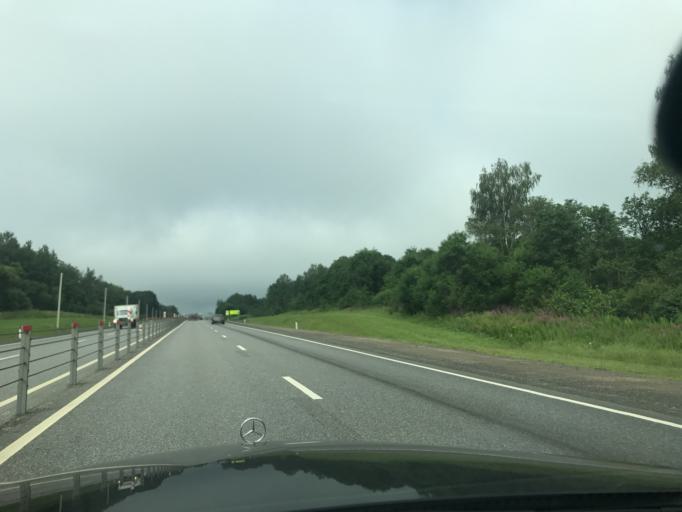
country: RU
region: Smolensk
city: Vyaz'ma
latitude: 55.2536
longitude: 34.3504
